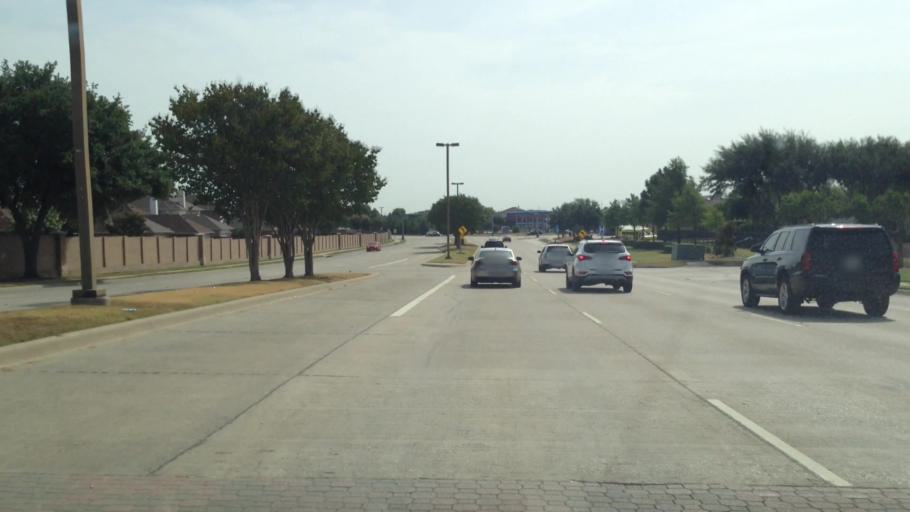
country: US
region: Texas
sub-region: Denton County
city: Lewisville
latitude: 33.0139
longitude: -96.9487
